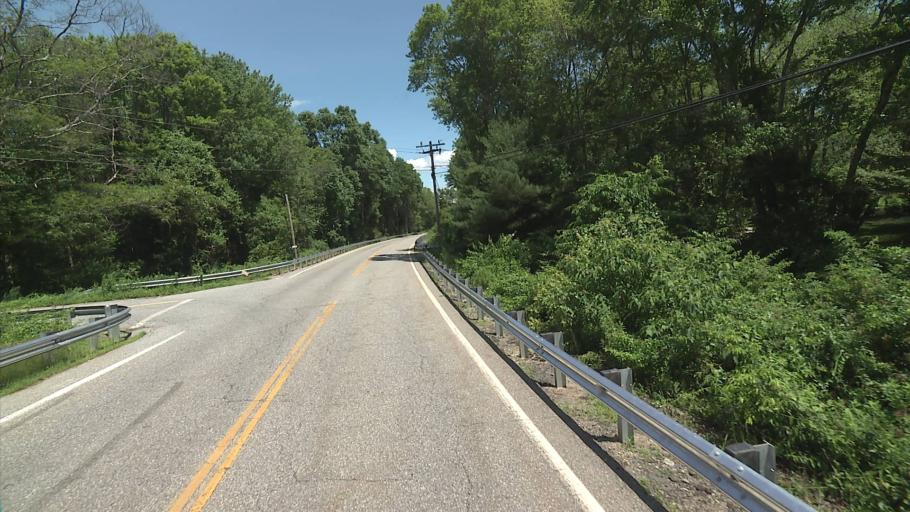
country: US
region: Connecticut
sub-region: New London County
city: Preston City
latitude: 41.5123
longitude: -71.8911
